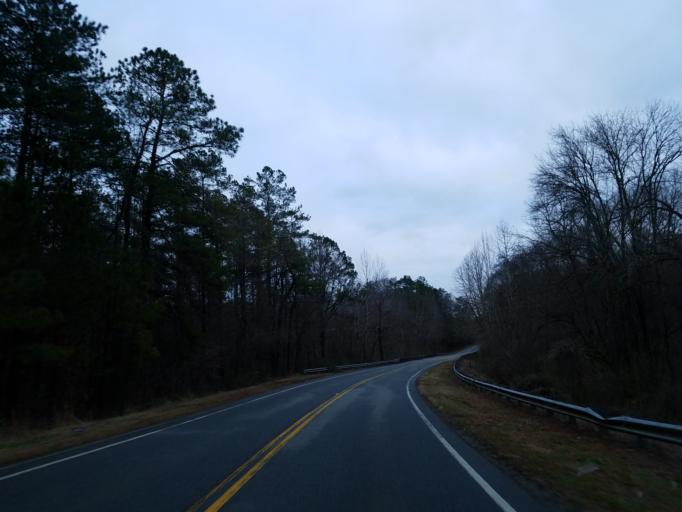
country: US
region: Georgia
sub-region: Bartow County
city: Emerson
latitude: 34.1020
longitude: -84.7384
